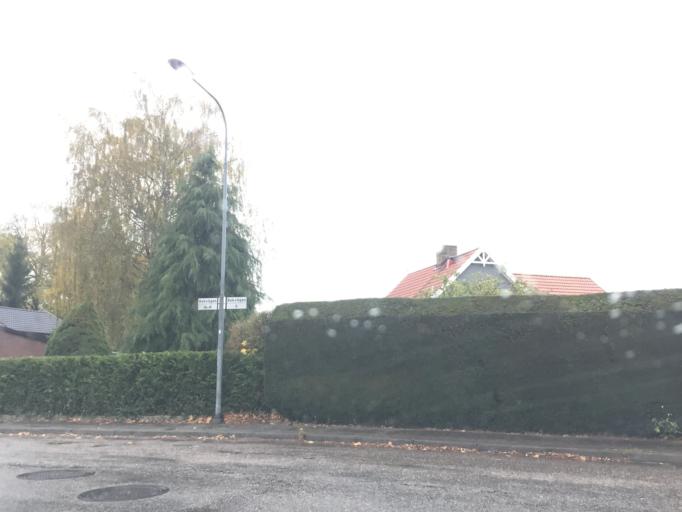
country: SE
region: Vaestra Goetaland
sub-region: Trollhattan
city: Trollhattan
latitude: 58.2898
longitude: 12.3474
